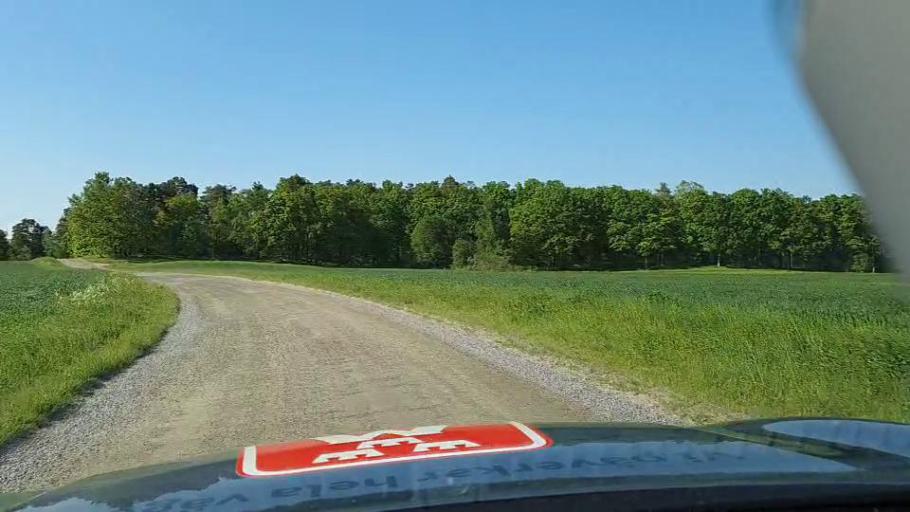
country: SE
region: Skane
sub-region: Hassleholms Kommun
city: Tormestorp
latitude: 56.1142
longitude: 13.7189
